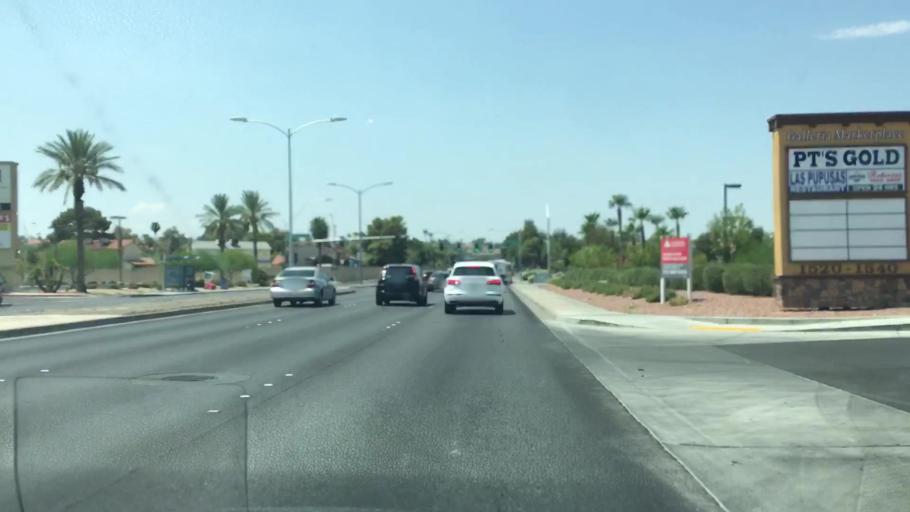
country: US
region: Nevada
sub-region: Clark County
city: Whitney
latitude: 36.0639
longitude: -115.0512
